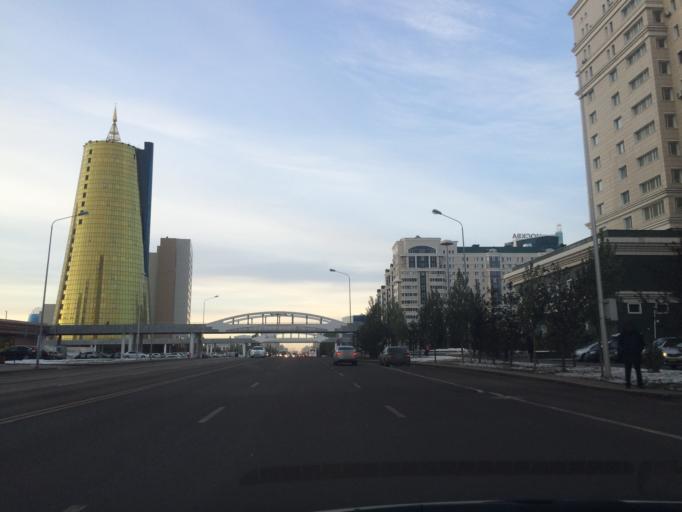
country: KZ
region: Astana Qalasy
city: Astana
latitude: 51.1285
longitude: 71.4389
